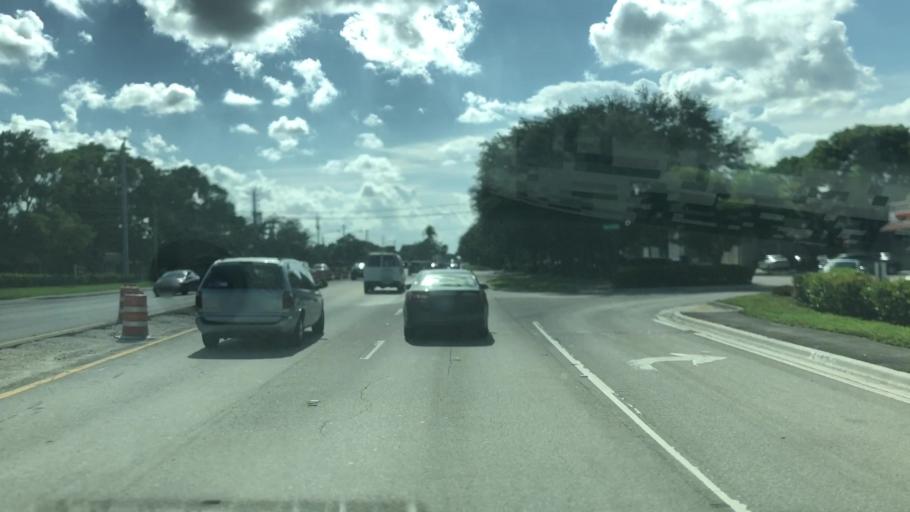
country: US
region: Florida
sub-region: Broward County
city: Parkland
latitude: 26.2868
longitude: -80.2352
